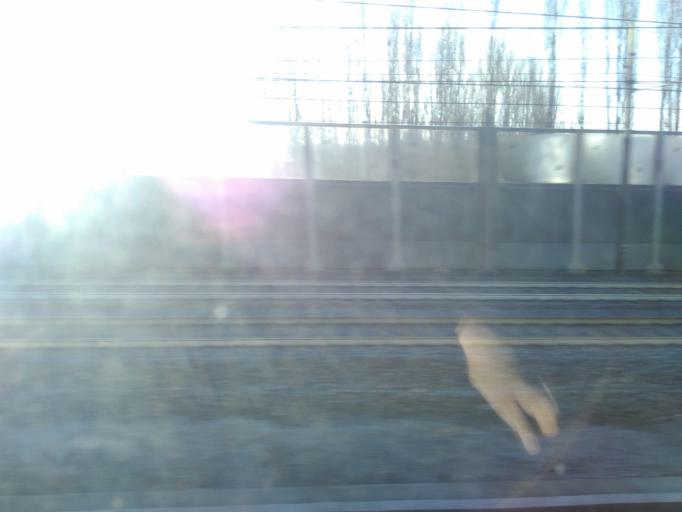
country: IT
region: Veneto
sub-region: Provincia di Padova
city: Vigonza
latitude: 45.4341
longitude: 11.9725
